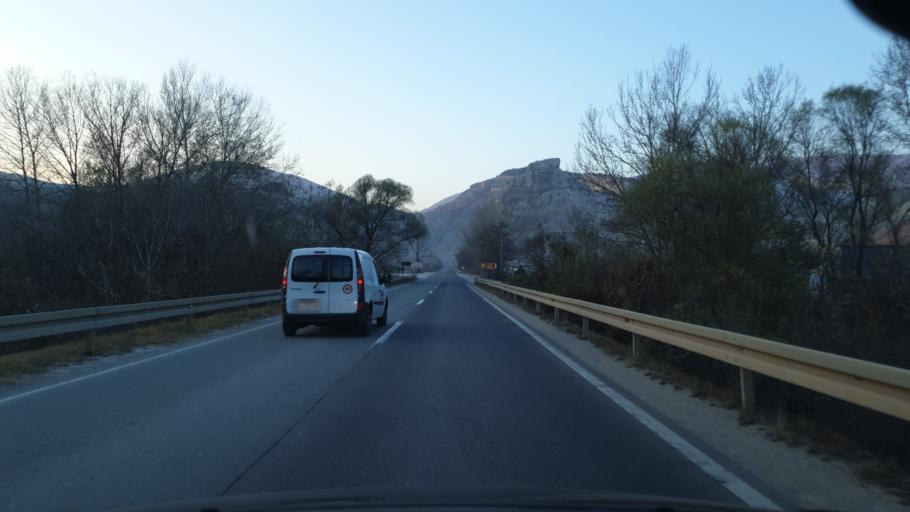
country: RS
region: Central Serbia
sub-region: Nisavski Okrug
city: Svrljig
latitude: 43.3017
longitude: 22.1955
